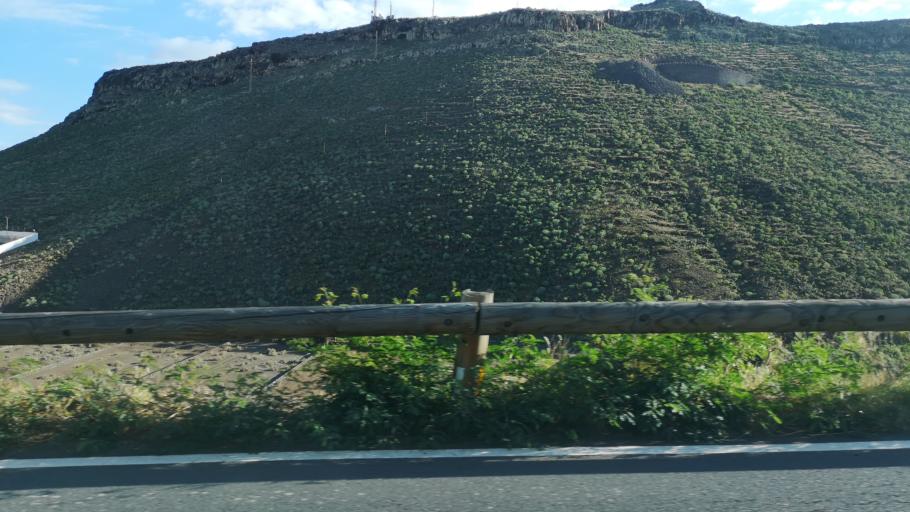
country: ES
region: Canary Islands
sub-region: Provincia de Santa Cruz de Tenerife
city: San Sebastian de la Gomera
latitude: 28.0900
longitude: -17.1210
